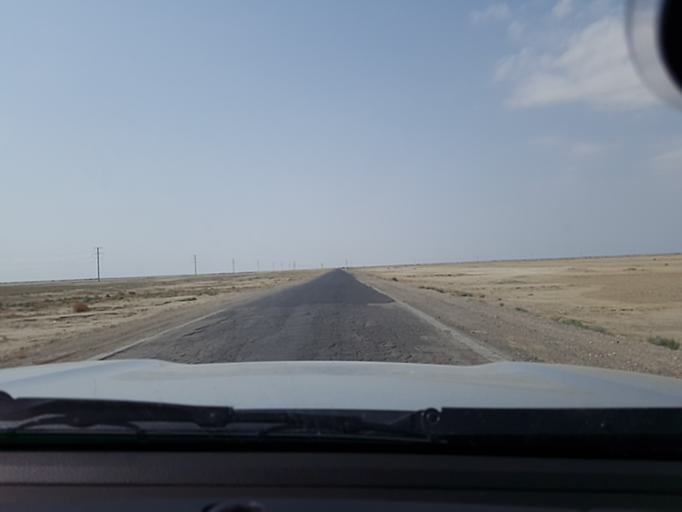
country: TM
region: Balkan
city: Gumdag
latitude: 39.0166
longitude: 54.5853
